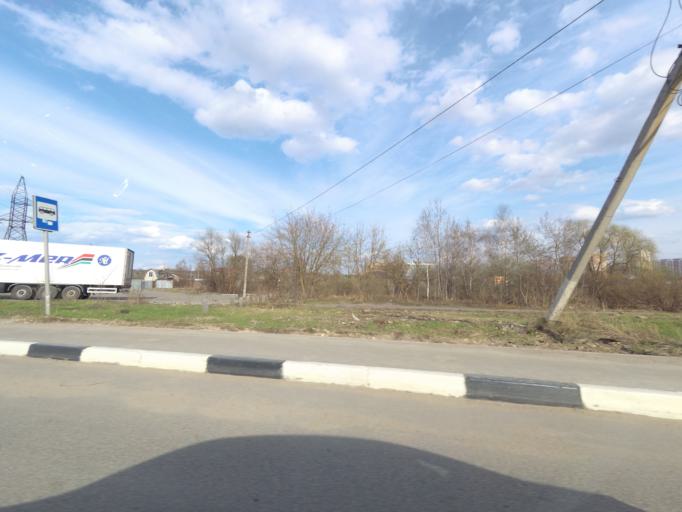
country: RU
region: Moskovskaya
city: Lobnya
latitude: 56.0079
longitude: 37.4373
